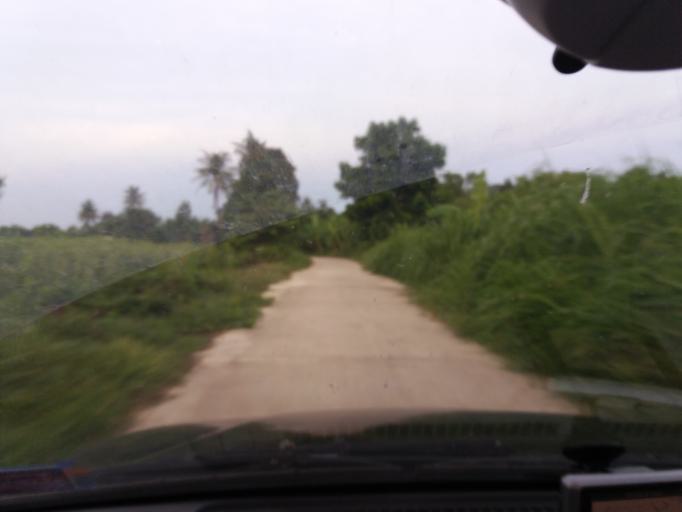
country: TH
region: Suphan Buri
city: Doembang Nangbuat
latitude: 14.8116
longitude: 100.1422
